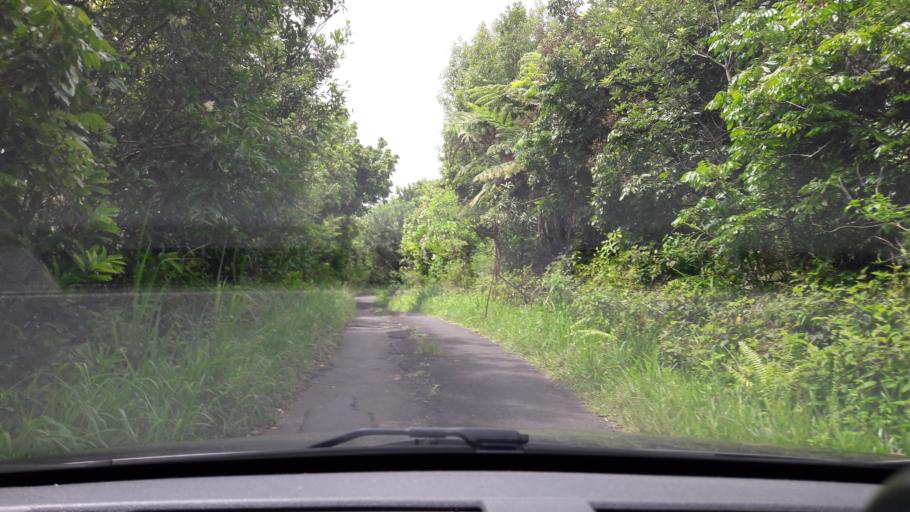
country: RE
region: Reunion
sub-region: Reunion
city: Saint-Benoit
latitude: -21.0996
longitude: 55.6963
